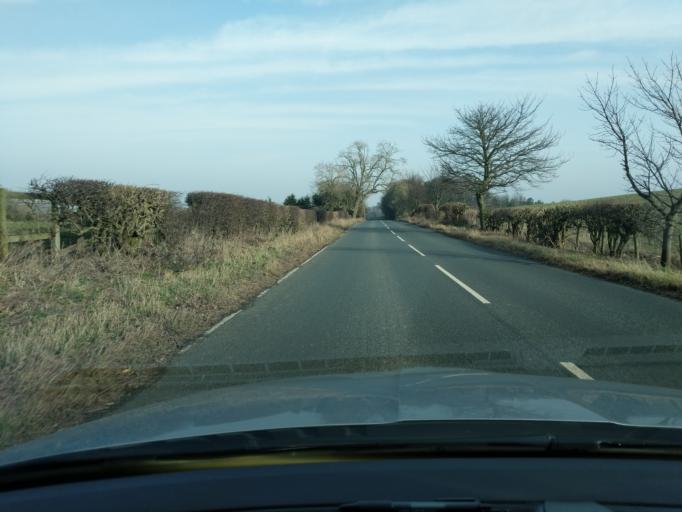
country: GB
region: England
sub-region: North Yorkshire
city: Catterick Garrison
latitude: 54.3471
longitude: -1.7047
